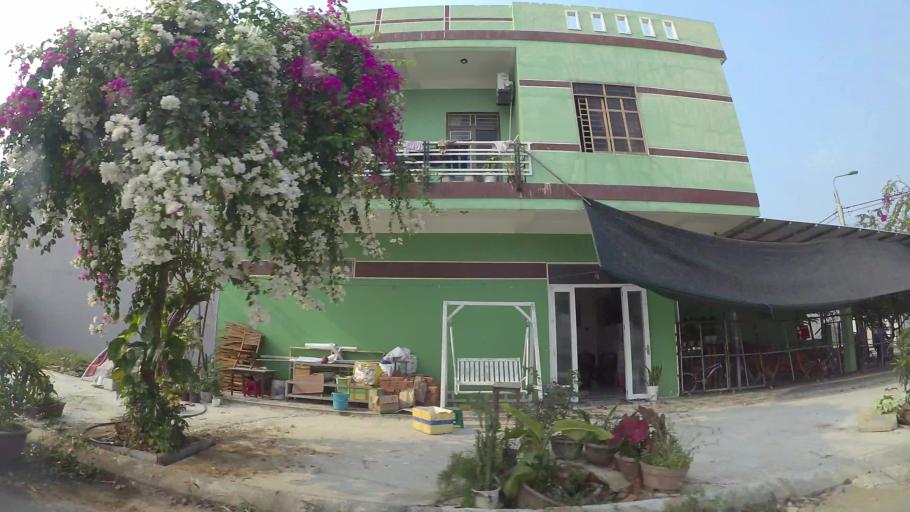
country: VN
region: Da Nang
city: Cam Le
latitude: 16.0083
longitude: 108.2269
